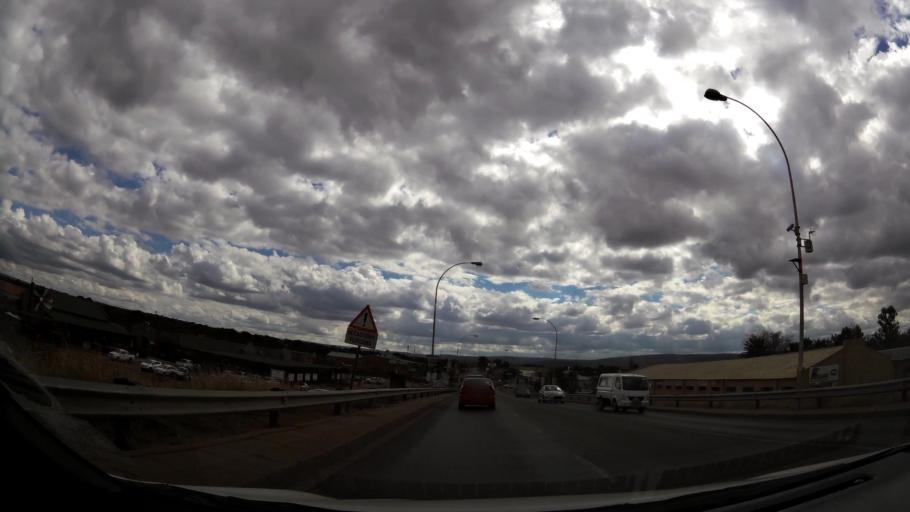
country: ZA
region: Limpopo
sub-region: Waterberg District Municipality
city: Modimolle
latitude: -24.7128
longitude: 28.4174
